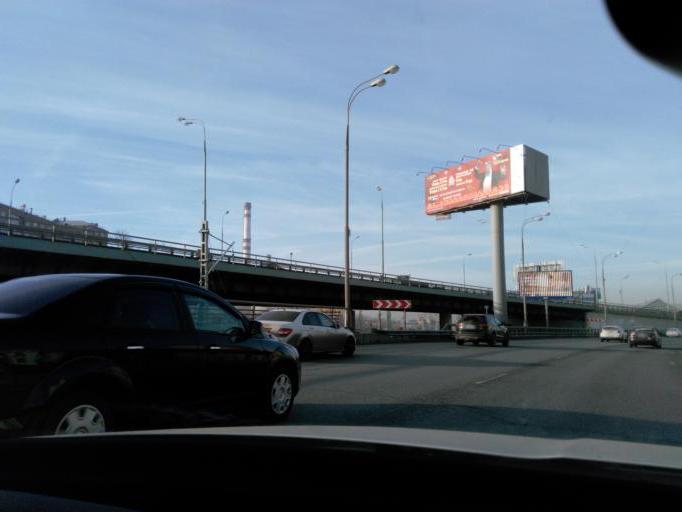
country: RU
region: Moskovskaya
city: Kozhukhovo
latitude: 55.7040
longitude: 37.6579
